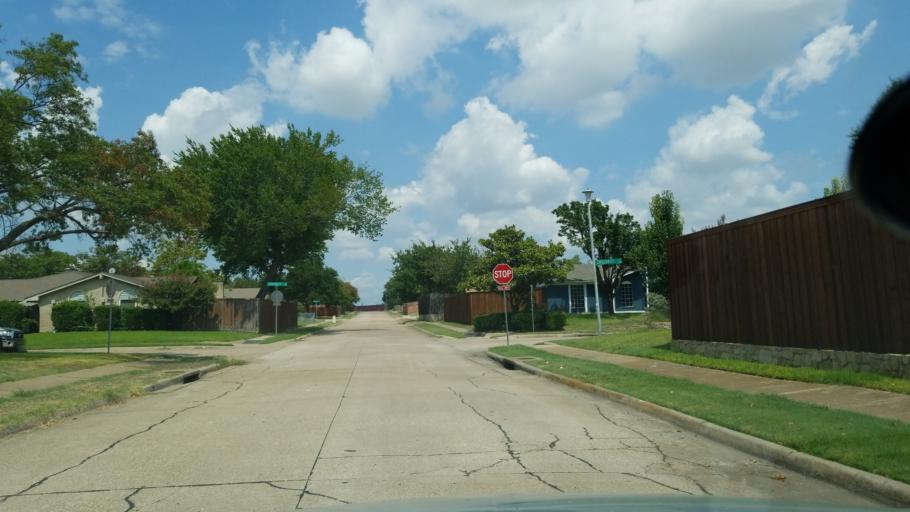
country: US
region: Texas
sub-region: Dallas County
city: Garland
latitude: 32.9262
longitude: -96.6533
